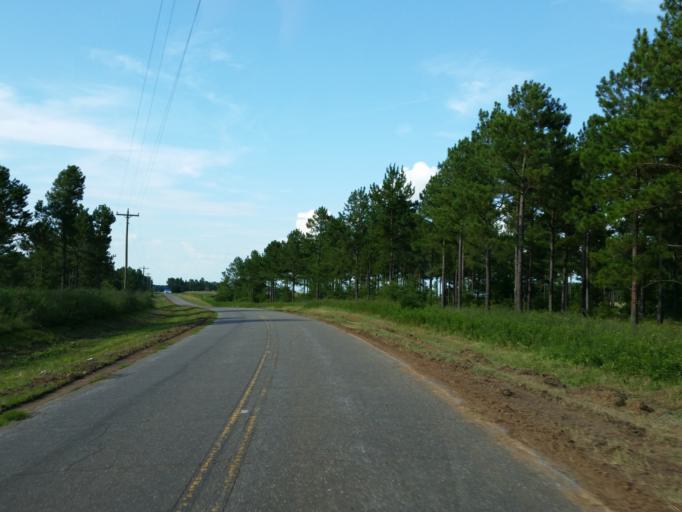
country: US
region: Georgia
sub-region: Crisp County
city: Cordele
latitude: 31.9171
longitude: -84.0117
